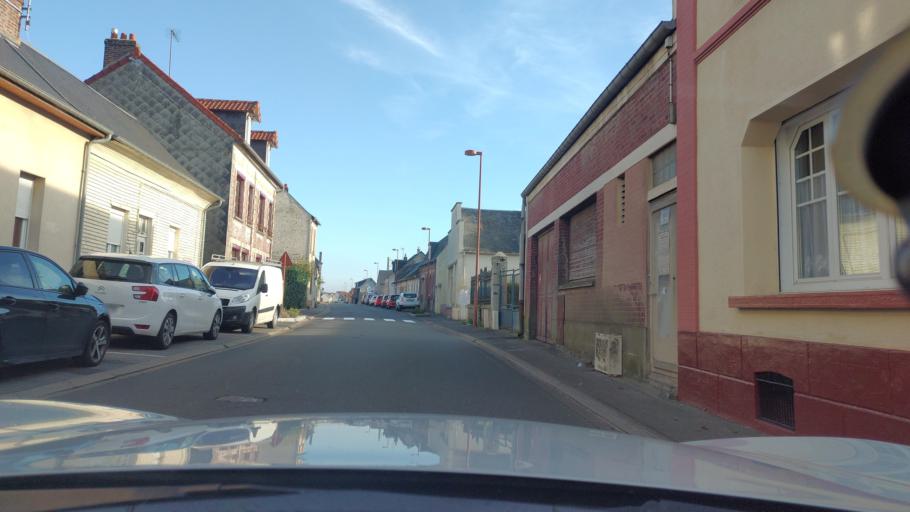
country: FR
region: Picardie
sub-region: Departement de la Somme
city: Fressenneville
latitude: 50.0672
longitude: 1.5787
